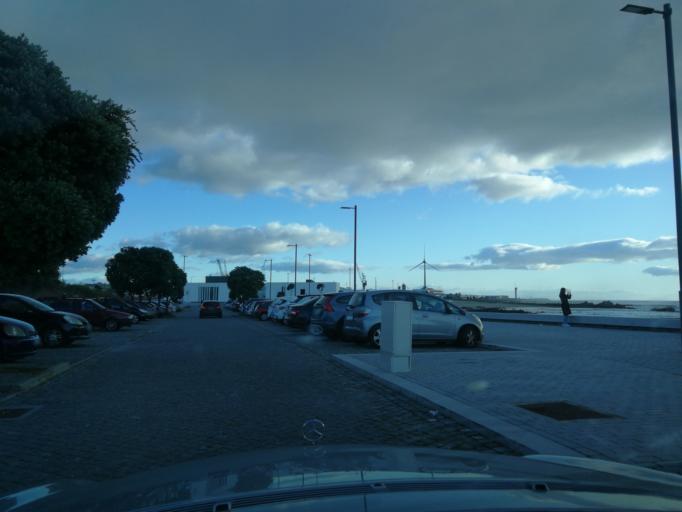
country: PT
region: Viana do Castelo
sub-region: Viana do Castelo
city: Viana do Castelo
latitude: 41.6978
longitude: -8.8515
